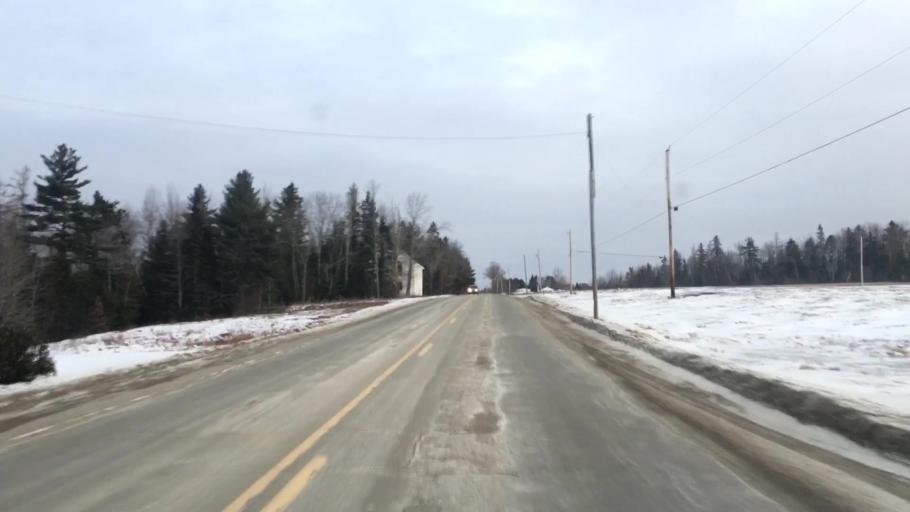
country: US
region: Maine
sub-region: Hancock County
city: Franklin
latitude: 44.7106
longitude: -68.3388
